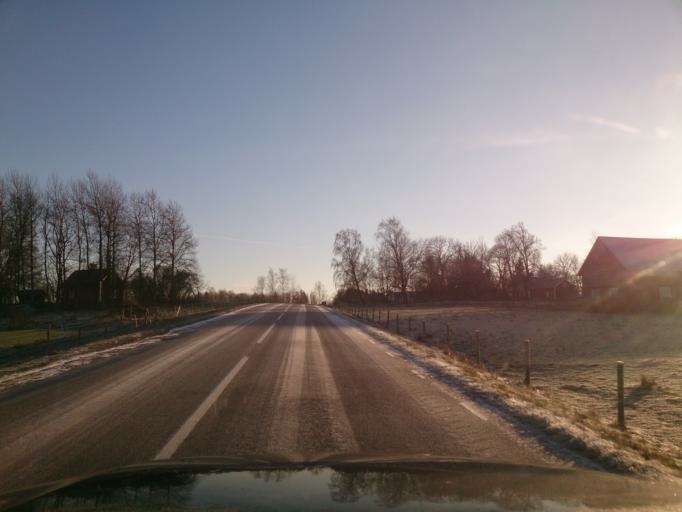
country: SE
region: OEstergoetland
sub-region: Linkopings Kommun
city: Linghem
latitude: 58.4294
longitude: 15.9041
